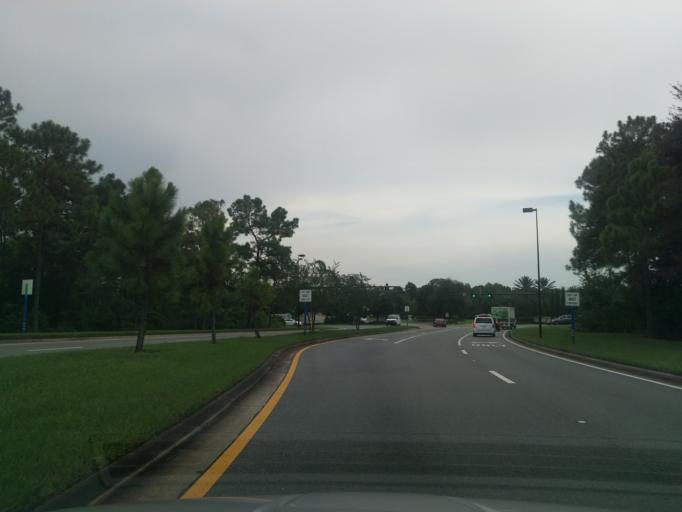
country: US
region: Florida
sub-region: Osceola County
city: Celebration
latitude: 28.3896
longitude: -81.5415
